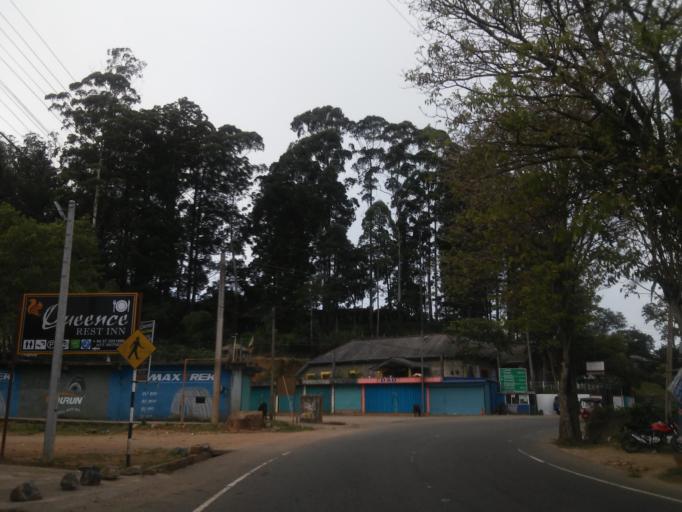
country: LK
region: Uva
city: Haputale
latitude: 6.7711
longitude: 80.9619
